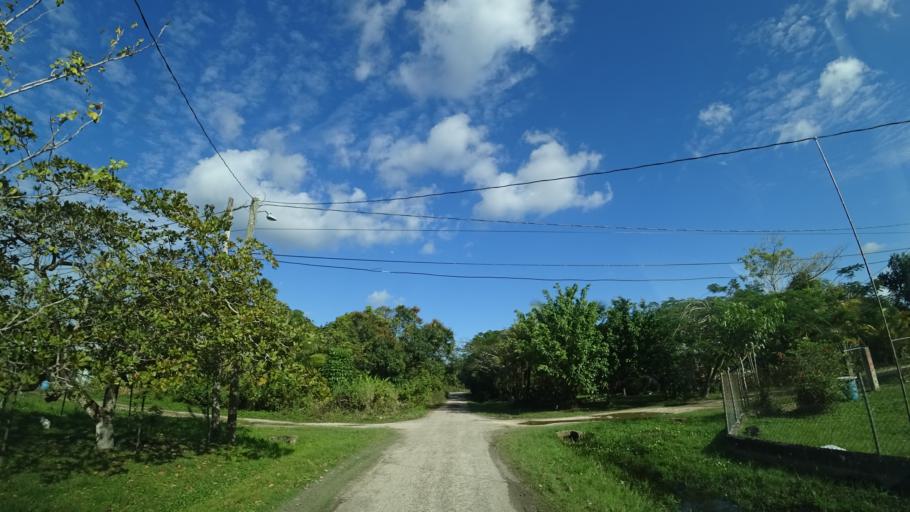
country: BZ
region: Belize
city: Belize City
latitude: 17.5647
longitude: -88.4075
